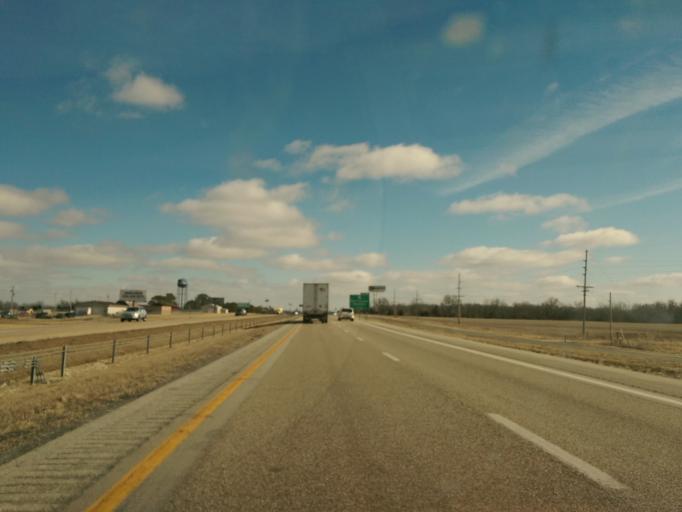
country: US
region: Missouri
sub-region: Montgomery County
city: Montgomery City
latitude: 38.9028
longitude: -91.4772
